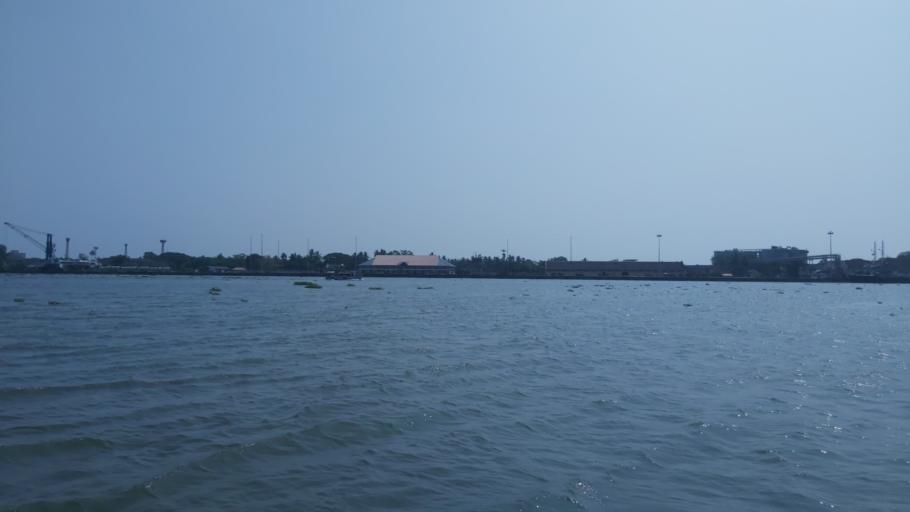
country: IN
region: Kerala
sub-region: Ernakulam
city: Cochin
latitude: 9.9711
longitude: 76.2694
